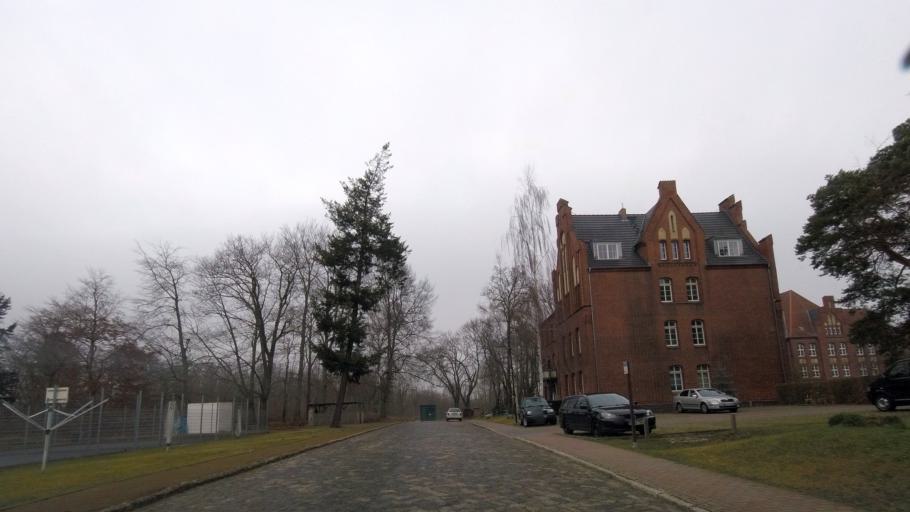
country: DE
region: Brandenburg
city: Juterbog
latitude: 51.9989
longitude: 13.0476
